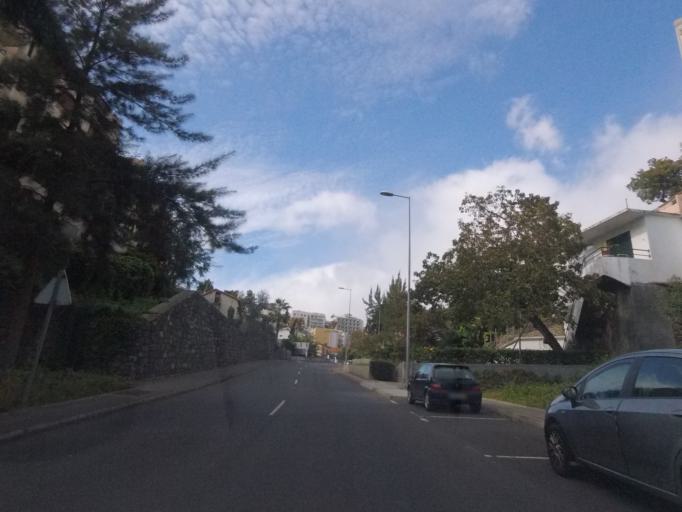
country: PT
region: Madeira
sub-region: Funchal
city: Funchal
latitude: 32.6478
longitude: -16.9251
